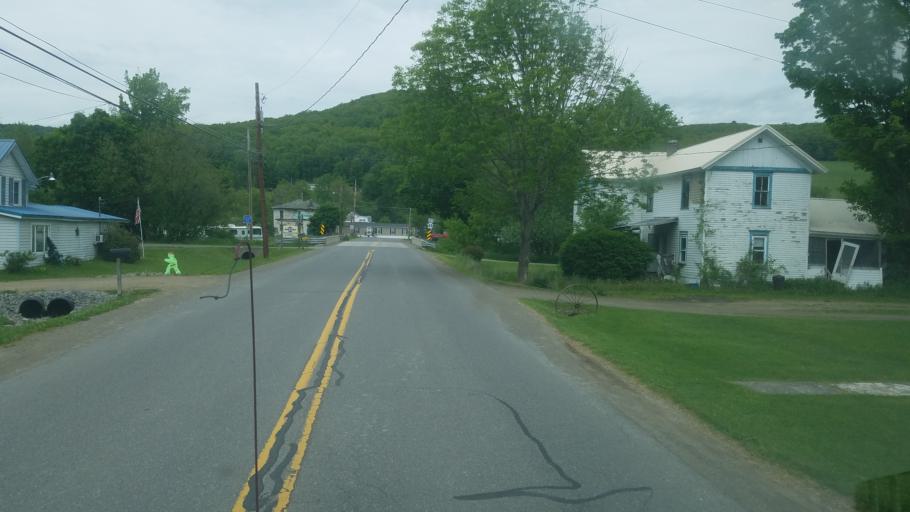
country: US
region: Pennsylvania
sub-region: Tioga County
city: Westfield
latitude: 41.9119
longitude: -77.6038
